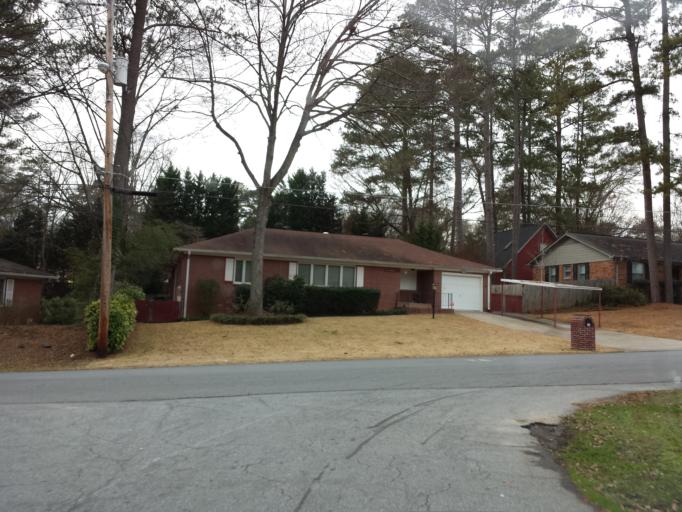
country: US
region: Georgia
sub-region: Cobb County
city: Marietta
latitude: 33.9474
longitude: -84.4935
